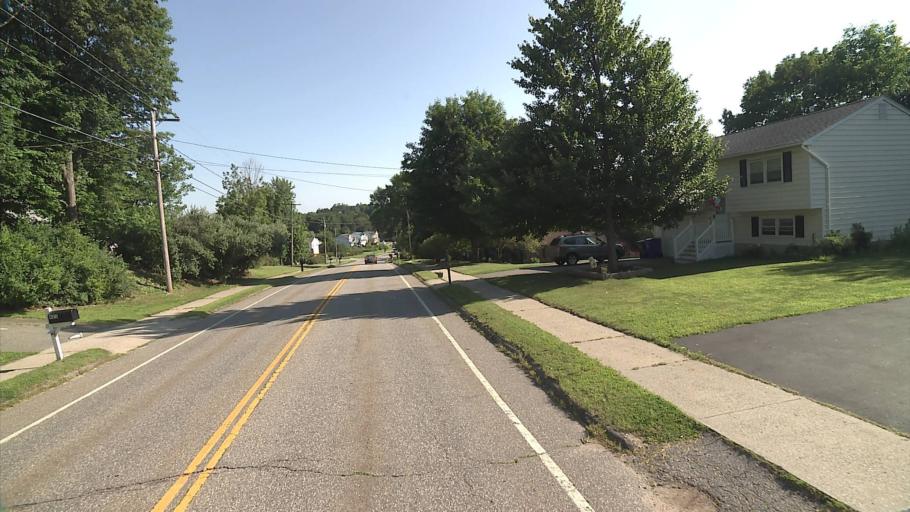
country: US
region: Connecticut
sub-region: Litchfield County
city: Northwest Harwinton
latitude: 41.8082
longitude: -73.0846
